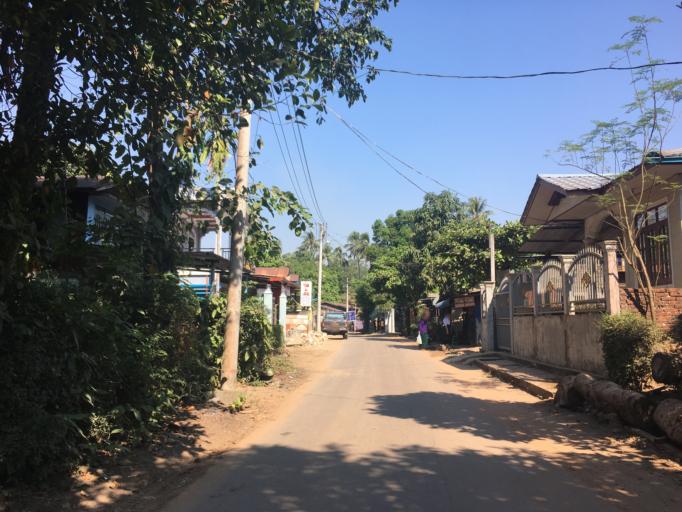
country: MM
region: Mon
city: Mawlamyine
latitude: 16.4337
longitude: 97.7054
